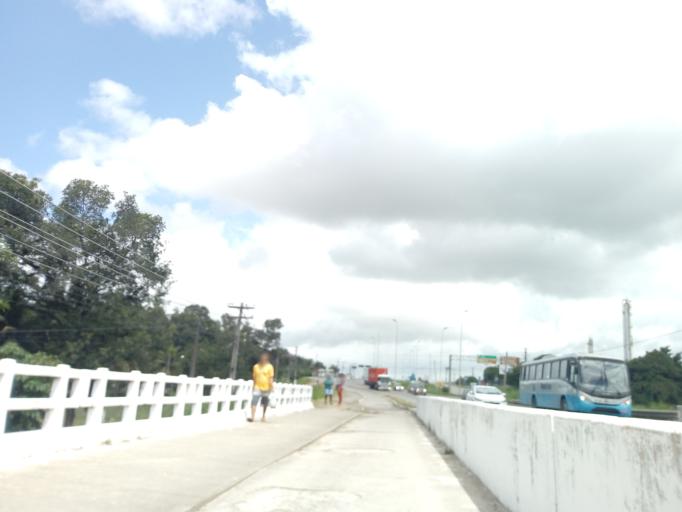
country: BR
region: Pernambuco
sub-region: Cabo De Santo Agostinho
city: Cabo
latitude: -8.2752
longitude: -35.0273
